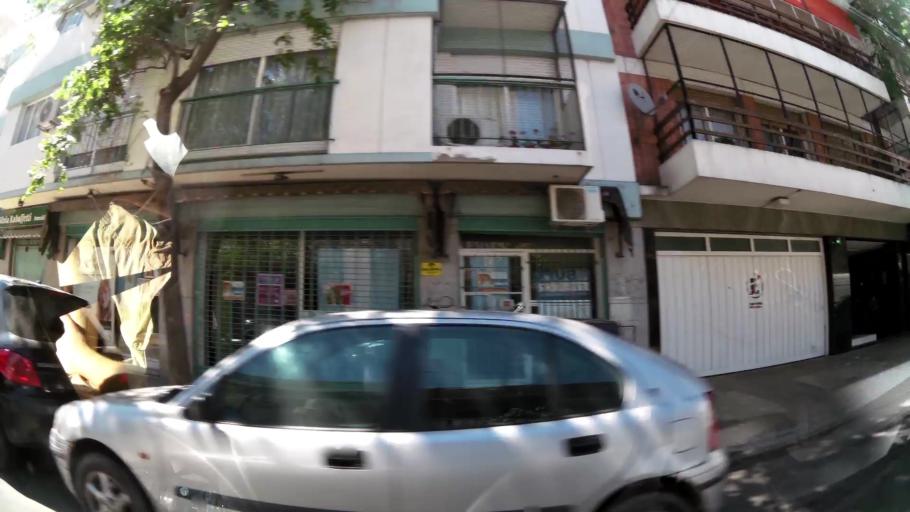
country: AR
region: Buenos Aires
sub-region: Partido de Vicente Lopez
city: Olivos
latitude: -34.5301
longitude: -58.4961
